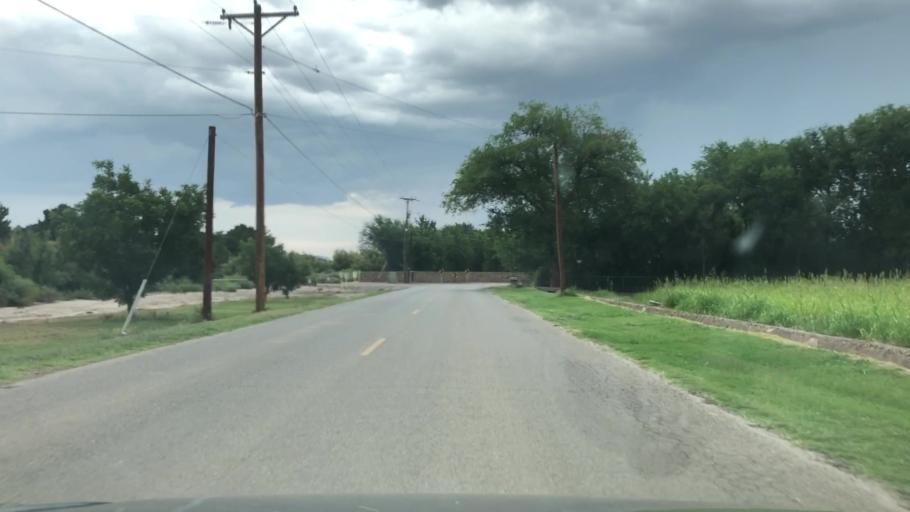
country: US
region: Texas
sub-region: El Paso County
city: Canutillo
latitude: 31.9083
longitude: -106.6353
